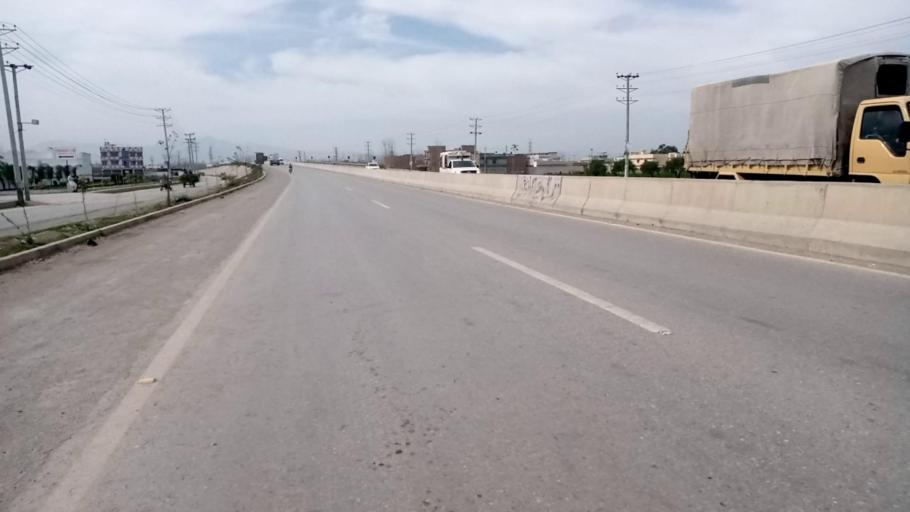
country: PK
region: Khyber Pakhtunkhwa
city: Peshawar
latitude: 34.0373
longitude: 71.6316
